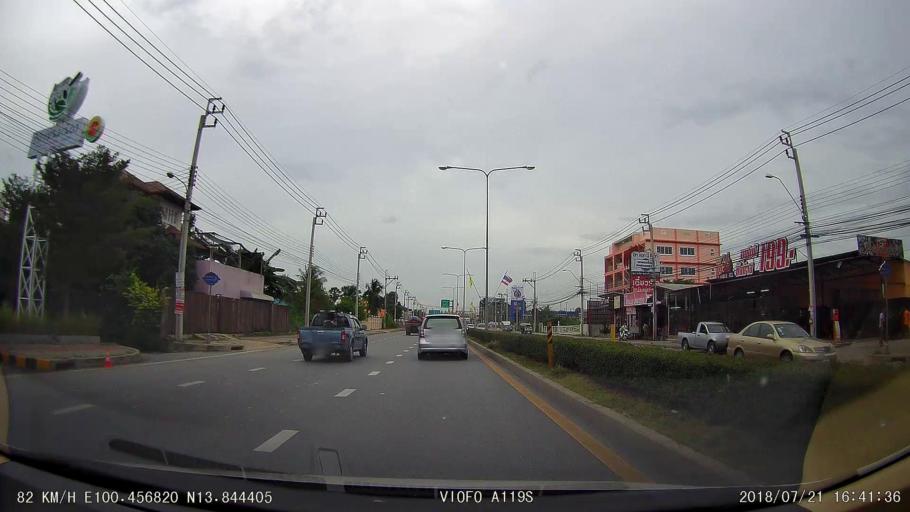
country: TH
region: Nonthaburi
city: Bang Kruai
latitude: 13.8444
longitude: 100.4568
